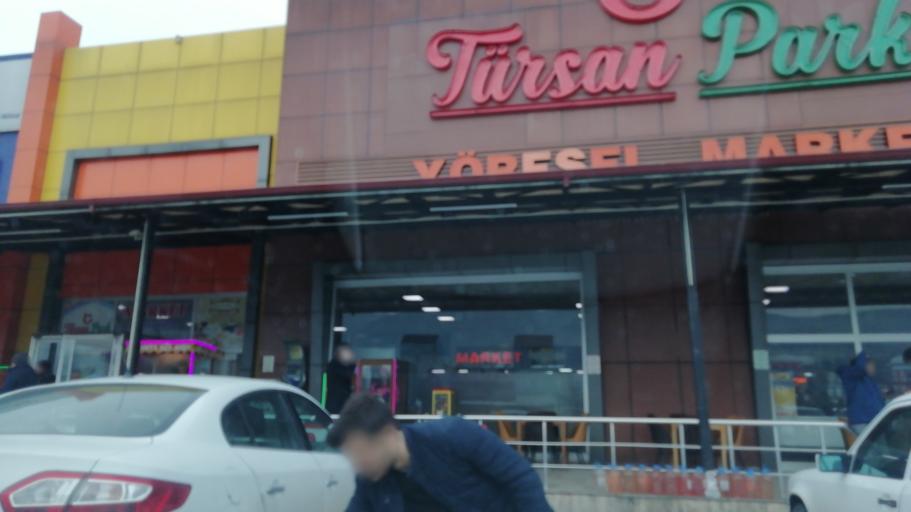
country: TR
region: Duzce
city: Kaynasli
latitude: 40.7916
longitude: 31.2411
